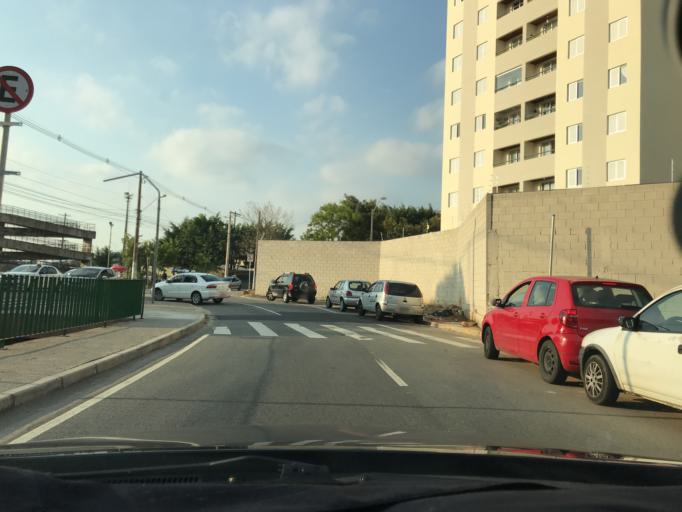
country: BR
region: Sao Paulo
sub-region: Osasco
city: Osasco
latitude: -23.5328
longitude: -46.7601
